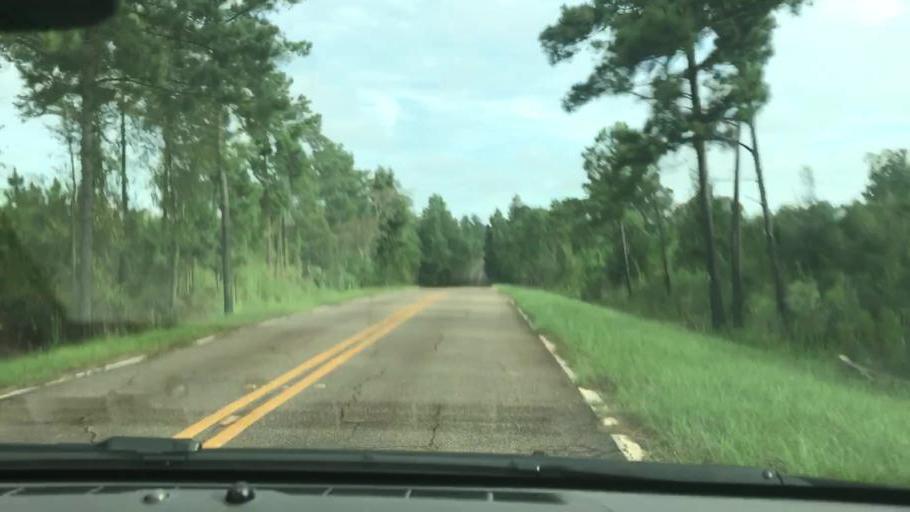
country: US
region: Georgia
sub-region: Stewart County
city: Lumpkin
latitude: 32.0567
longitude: -84.9032
